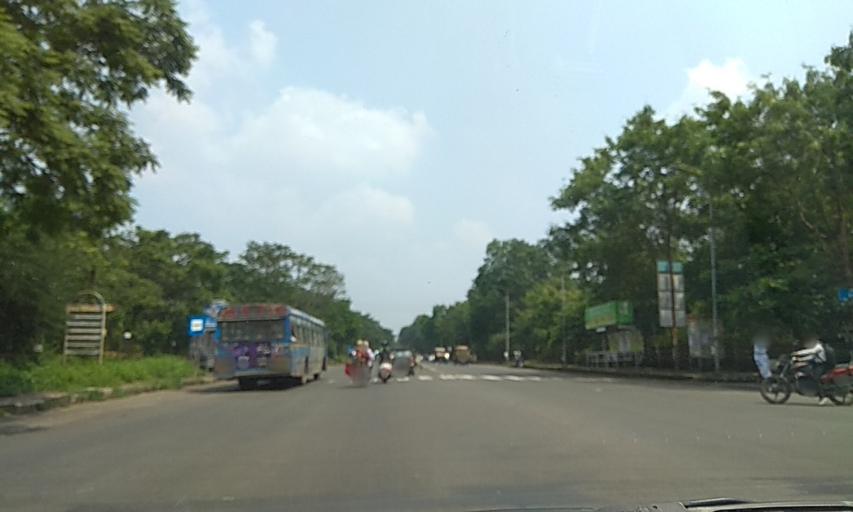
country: IN
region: Maharashtra
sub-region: Pune Division
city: Shivaji Nagar
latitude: 18.5391
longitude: 73.8093
